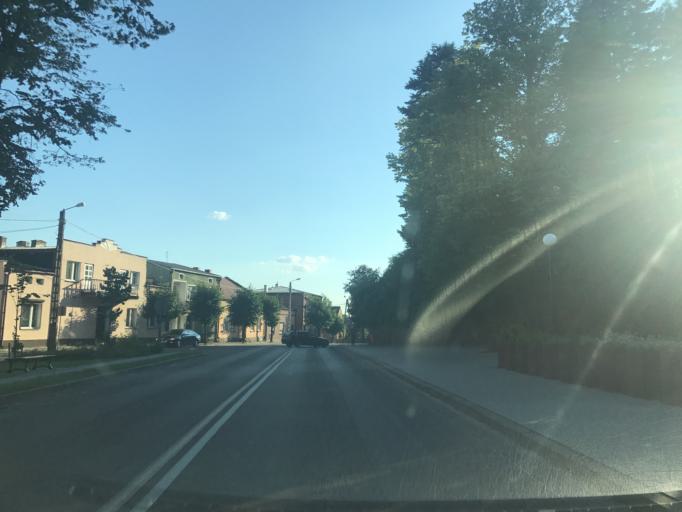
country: PL
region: Greater Poland Voivodeship
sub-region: Powiat turecki
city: Tuliszkow
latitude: 52.0769
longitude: 18.2972
